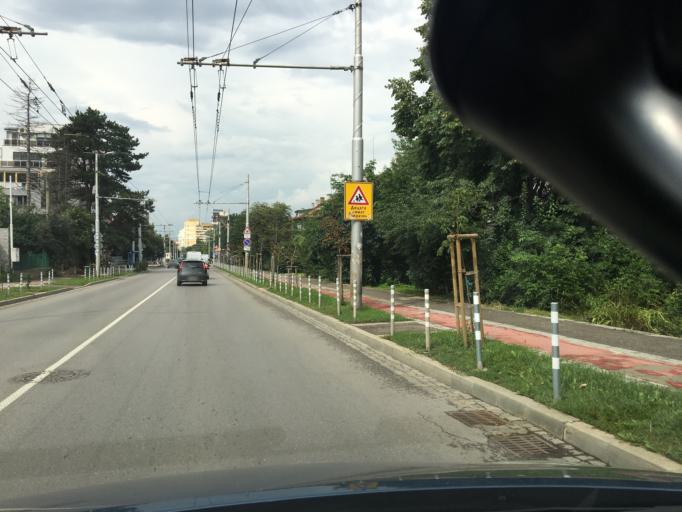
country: BG
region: Sofia-Capital
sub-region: Stolichna Obshtina
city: Sofia
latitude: 42.6638
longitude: 23.2746
